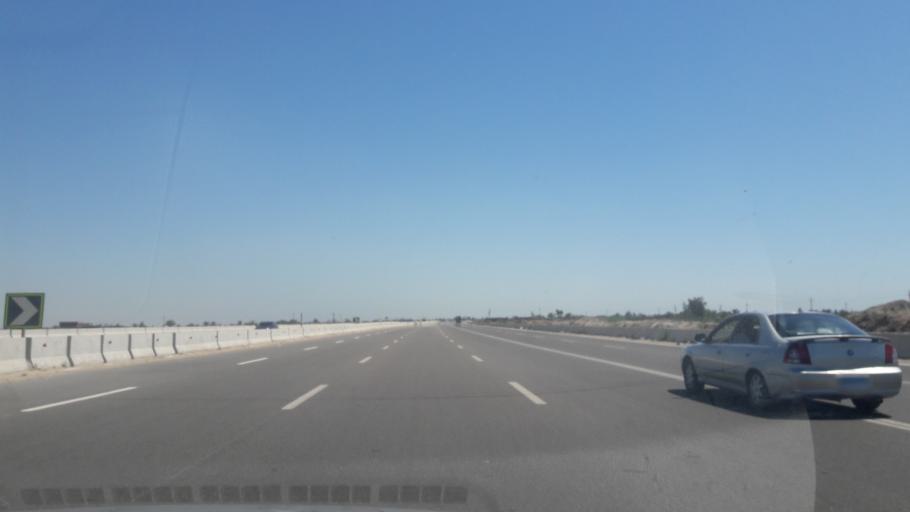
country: EG
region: Muhafazat Bur Sa`id
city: Port Said
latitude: 31.1606
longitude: 32.2355
